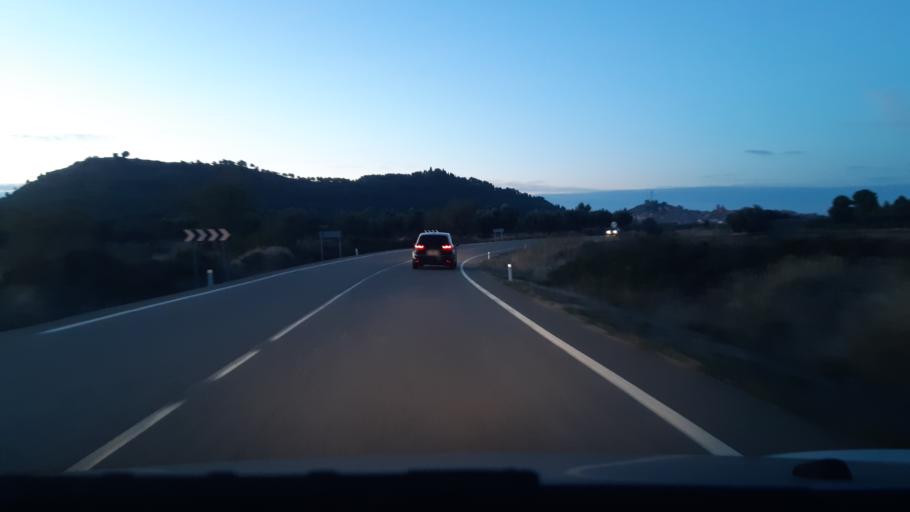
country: ES
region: Aragon
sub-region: Provincia de Teruel
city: Calaceite
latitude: 41.0010
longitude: 0.1940
